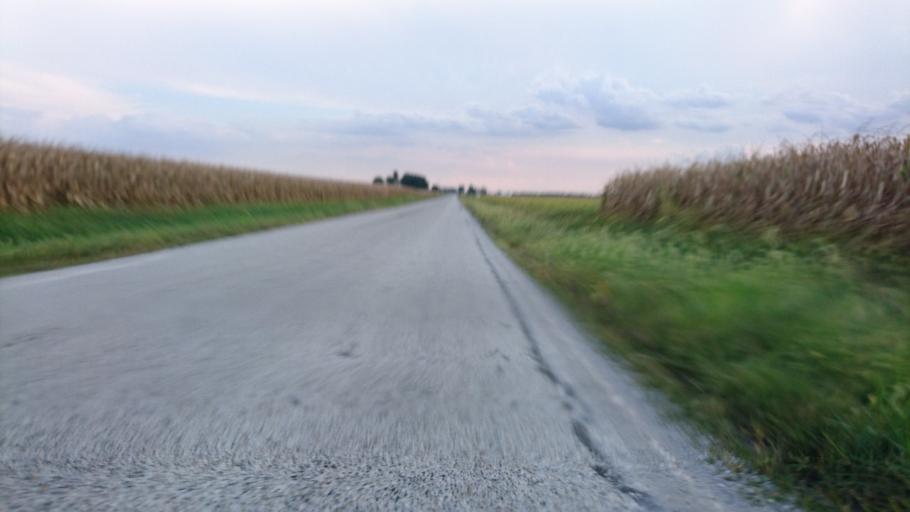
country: US
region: Illinois
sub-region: Logan County
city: Atlanta
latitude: 40.2489
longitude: -89.2051
